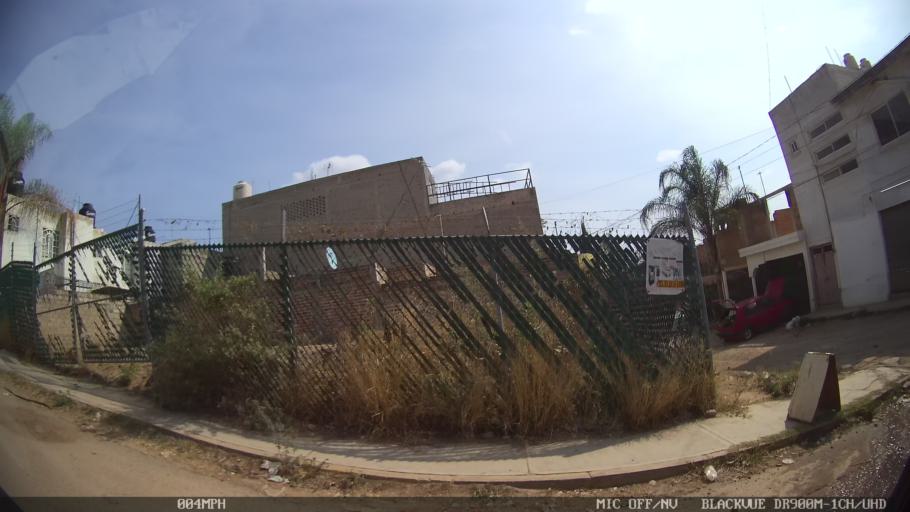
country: MX
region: Jalisco
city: Tonala
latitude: 20.6415
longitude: -103.2313
